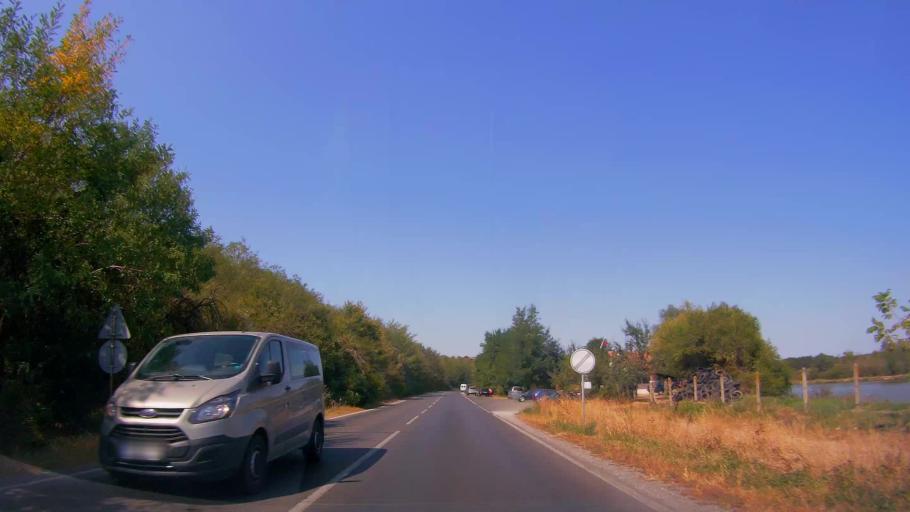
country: BG
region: Razgrad
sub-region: Obshtina Tsar Kaloyan
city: Tsar Kaloyan
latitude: 43.6170
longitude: 26.2136
